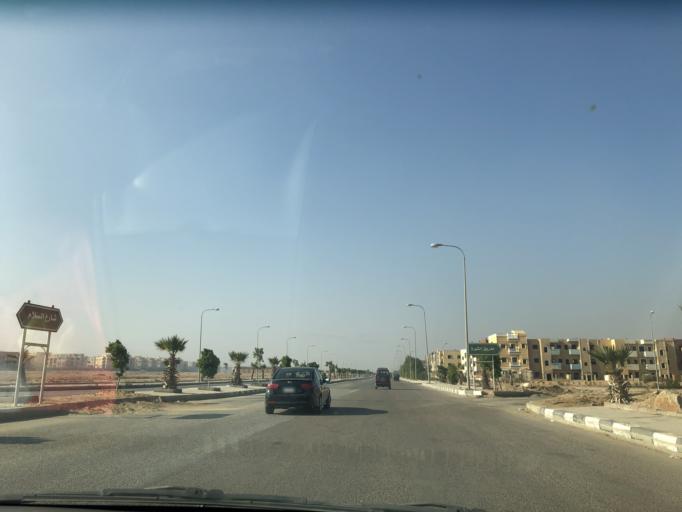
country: EG
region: Al Jizah
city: Madinat Sittah Uktubar
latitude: 29.9255
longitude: 31.0533
